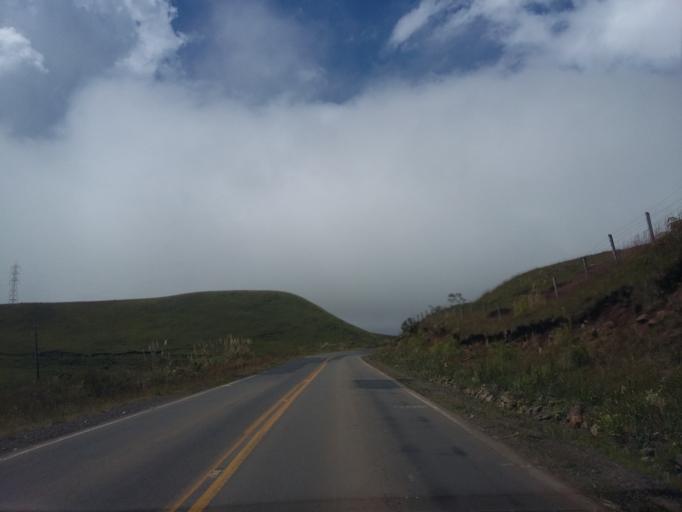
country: BR
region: Santa Catarina
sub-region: Lauro Muller
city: Lauro Muller
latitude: -28.3719
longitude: -49.5655
